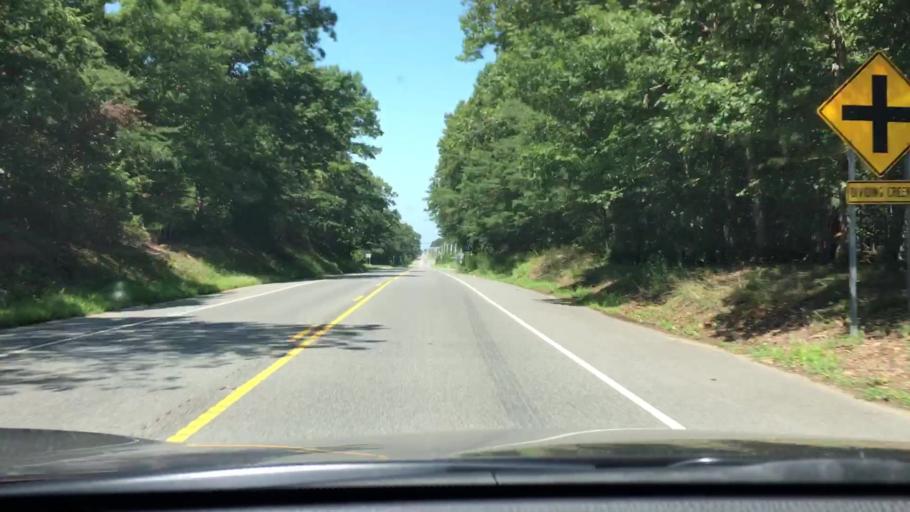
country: US
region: New Jersey
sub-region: Cumberland County
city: Laurel Lake
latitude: 39.3519
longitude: -75.0567
